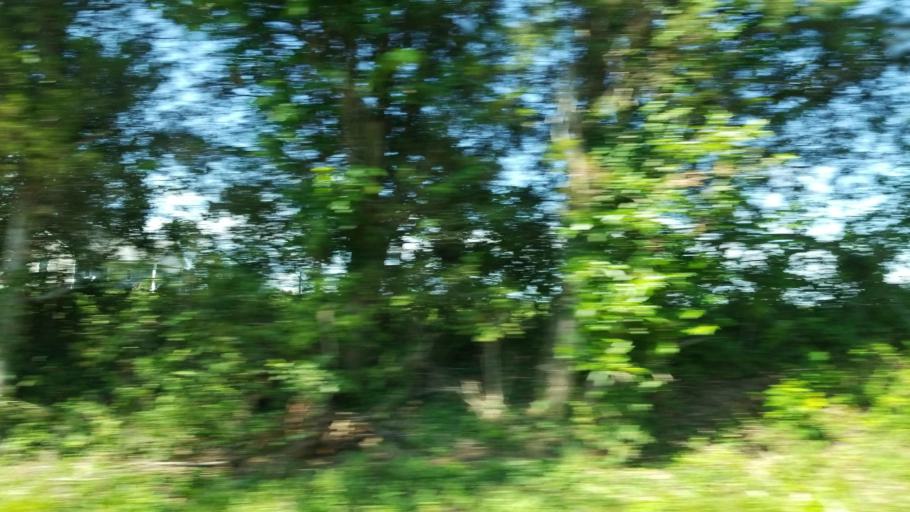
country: US
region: Illinois
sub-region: Williamson County
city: Johnston City
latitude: 37.7868
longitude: -88.7825
